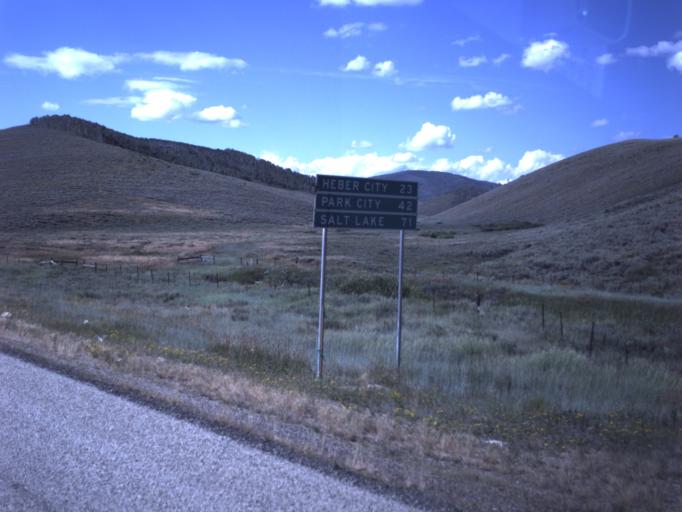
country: US
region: Utah
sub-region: Wasatch County
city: Heber
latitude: 40.2436
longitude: -111.1860
